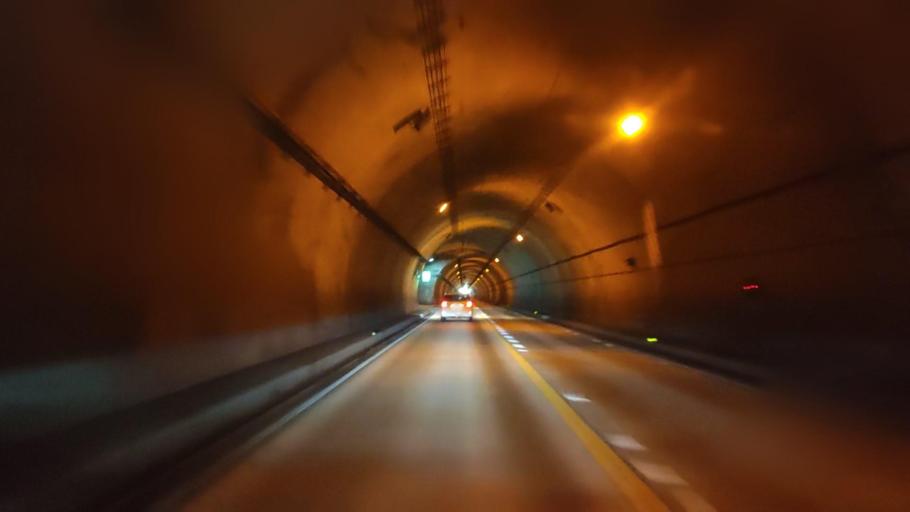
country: JP
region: Nara
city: Yoshino-cho
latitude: 34.2566
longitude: 135.9999
